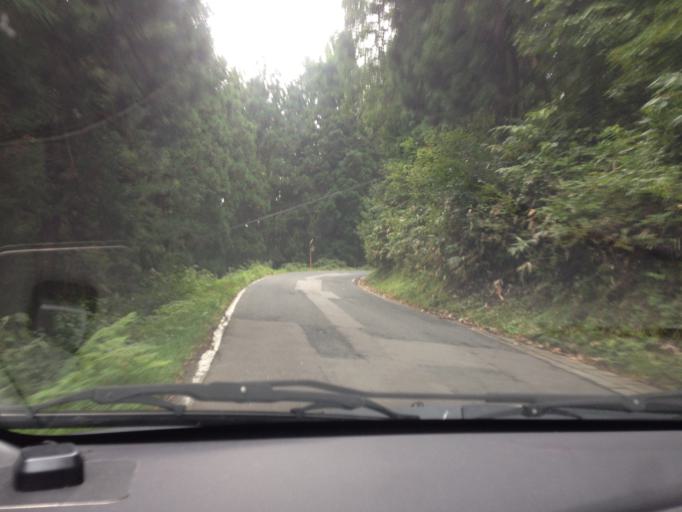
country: JP
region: Fukushima
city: Kitakata
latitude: 37.4855
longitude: 139.6912
